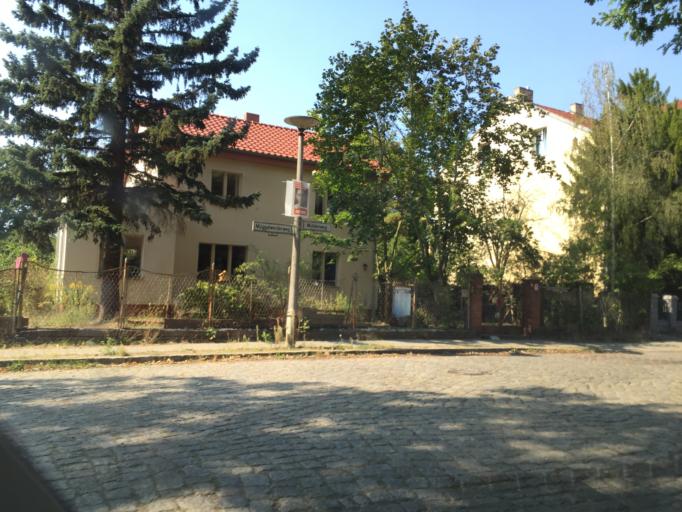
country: DE
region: Berlin
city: Rahnsdorf
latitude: 52.4396
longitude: 13.6883
